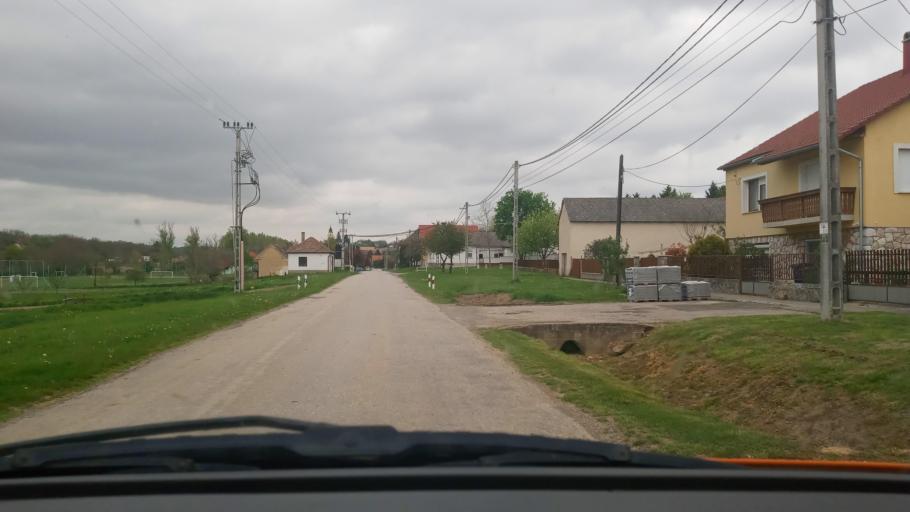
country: HU
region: Baranya
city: Boly
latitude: 45.9998
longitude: 18.5548
